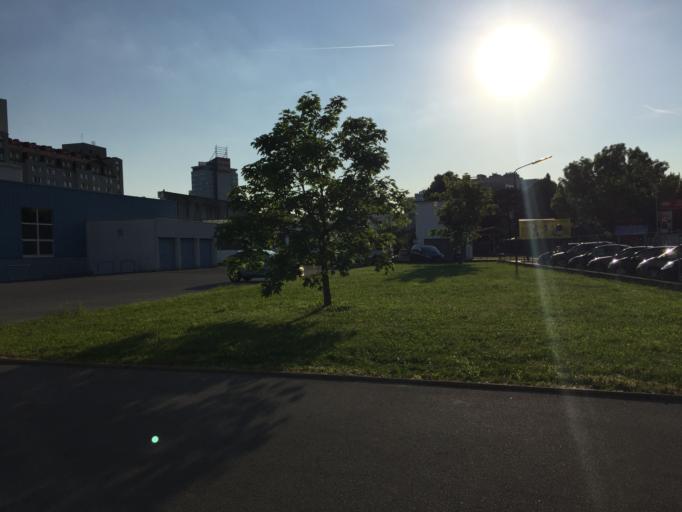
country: AT
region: Vienna
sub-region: Wien Stadt
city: Vienna
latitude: 48.2464
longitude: 16.3723
